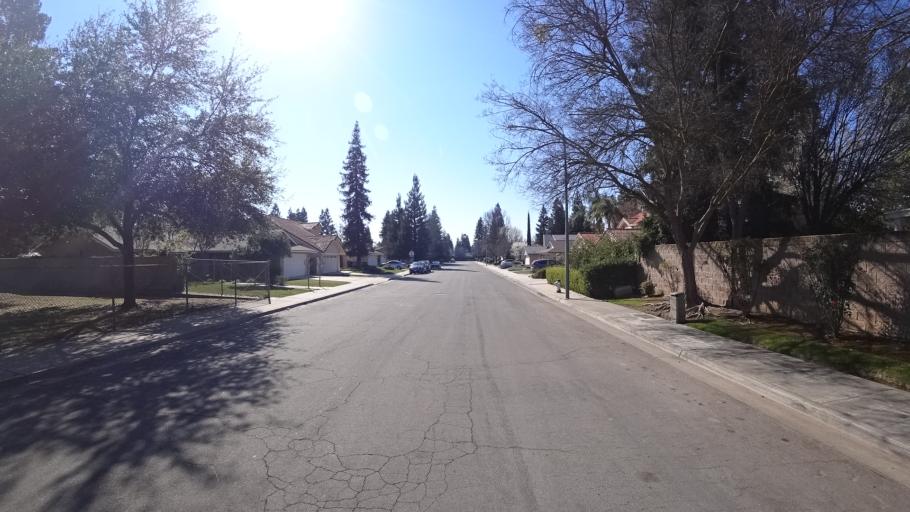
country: US
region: California
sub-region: Fresno County
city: Clovis
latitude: 36.8759
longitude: -119.7513
